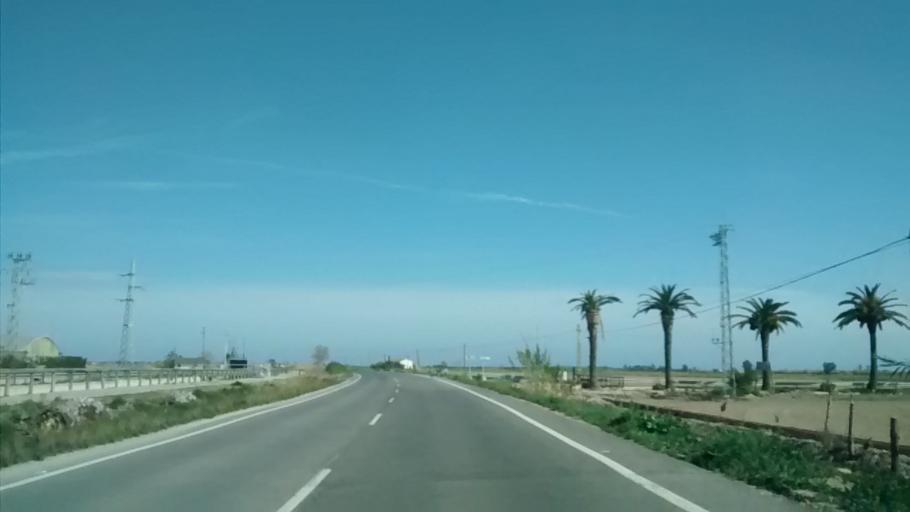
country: ES
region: Catalonia
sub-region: Provincia de Tarragona
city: Deltebre
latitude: 40.7070
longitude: 0.7648
